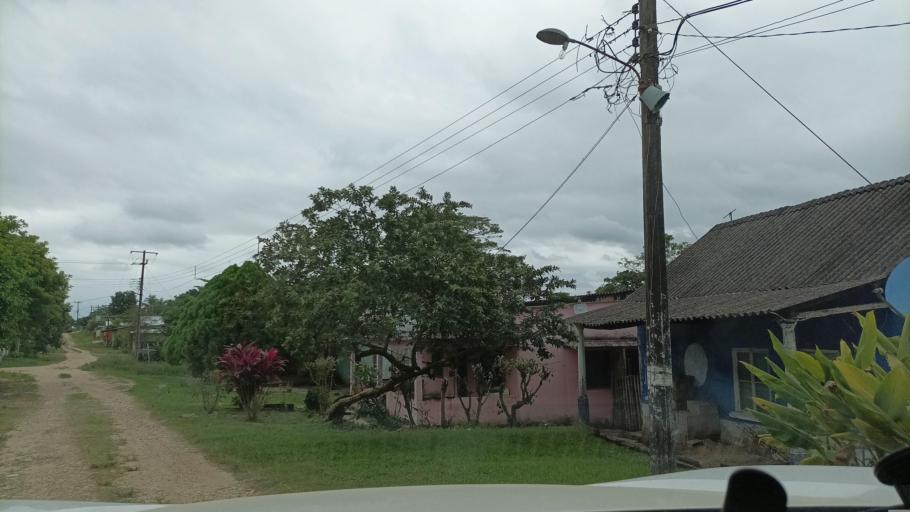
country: MX
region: Veracruz
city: Hidalgotitlan
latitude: 17.8086
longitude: -94.5420
